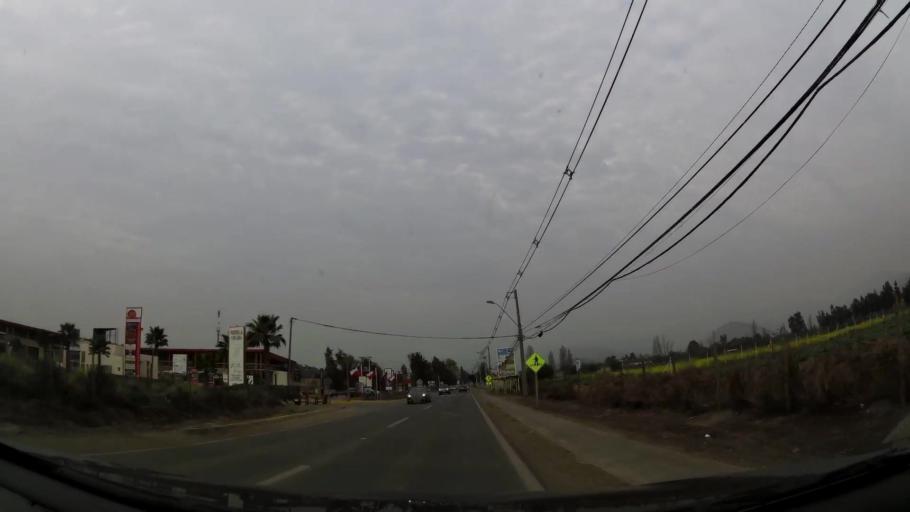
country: CL
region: Santiago Metropolitan
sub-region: Provincia de Chacabuco
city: Chicureo Abajo
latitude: -33.2857
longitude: -70.6852
